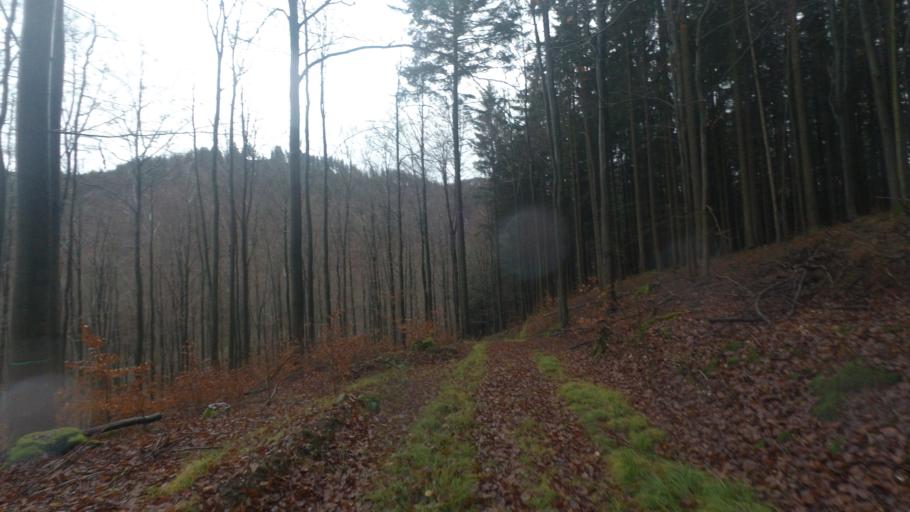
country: DE
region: Thuringia
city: Grafenroda
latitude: 50.7239
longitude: 10.7923
